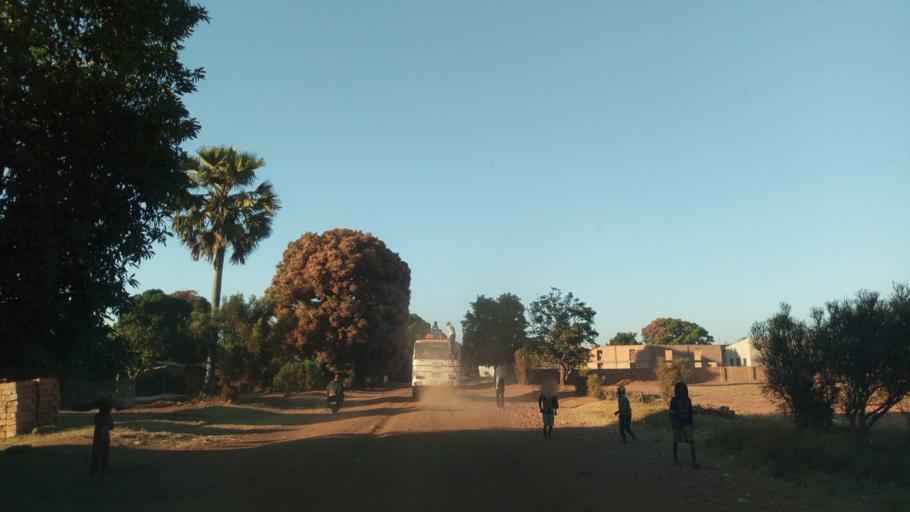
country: ZM
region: Luapula
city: Mwense
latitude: -10.3793
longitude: 28.6141
